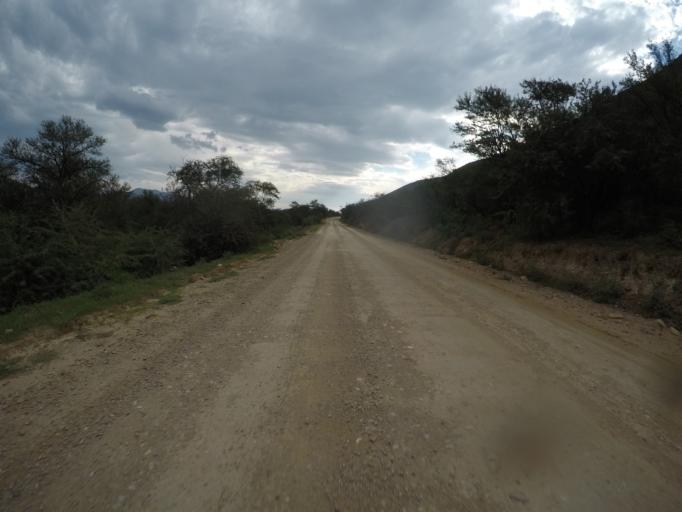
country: ZA
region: Eastern Cape
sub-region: Cacadu District Municipality
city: Kareedouw
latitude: -33.5733
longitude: 24.1340
